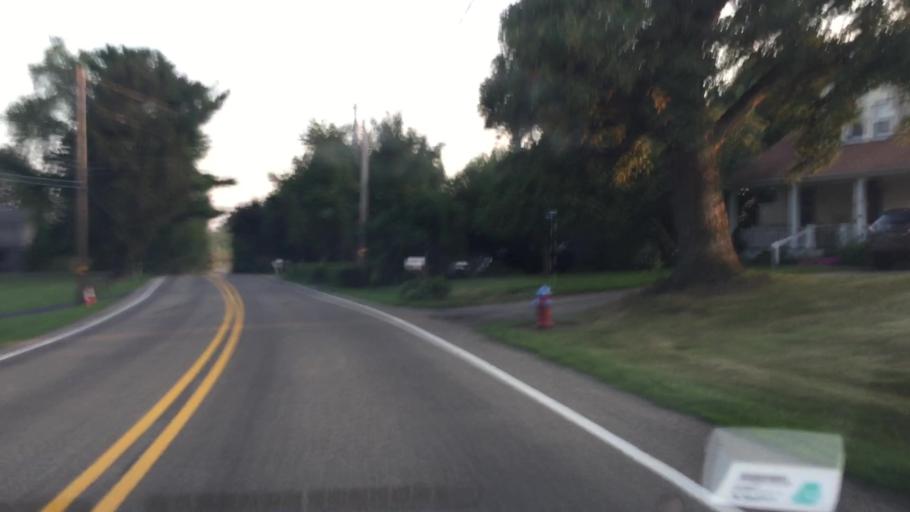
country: US
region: Pennsylvania
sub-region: Butler County
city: Fox Run
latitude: 40.7146
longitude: -80.0784
